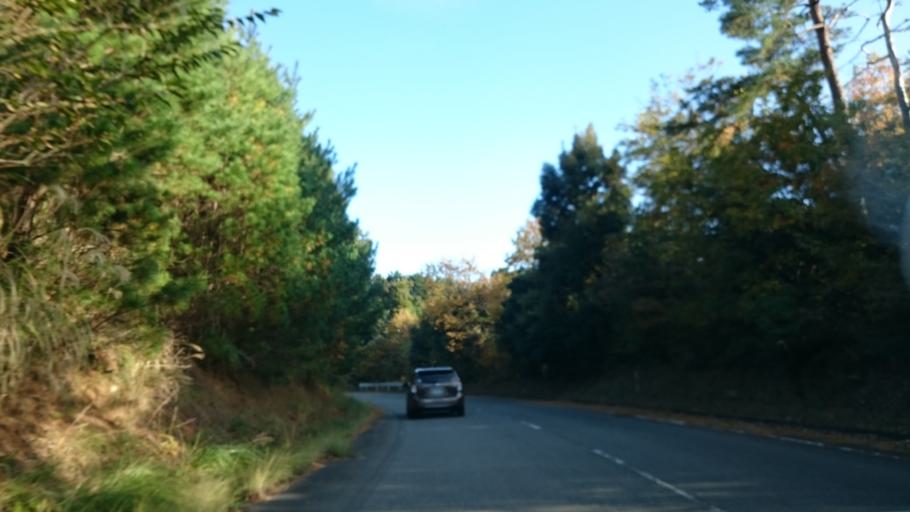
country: JP
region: Shizuoka
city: Heda
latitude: 34.9756
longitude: 138.8981
